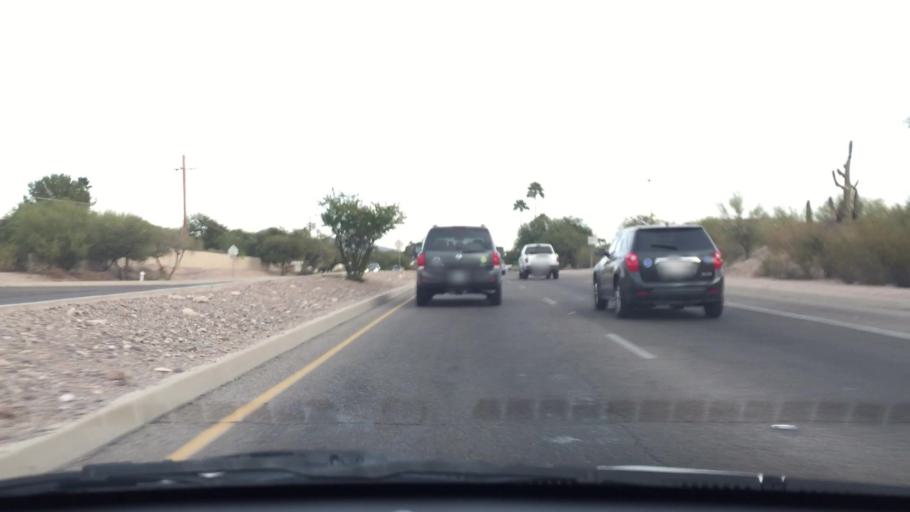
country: US
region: Arizona
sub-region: Pima County
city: Catalina Foothills
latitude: 32.3083
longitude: -110.8982
